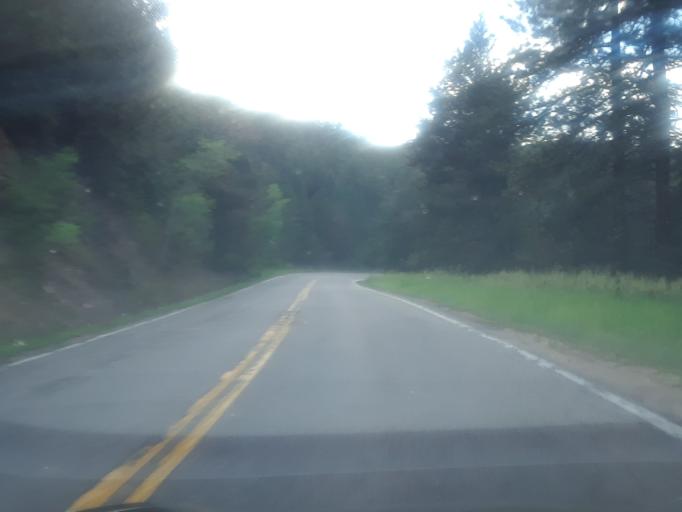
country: US
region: Colorado
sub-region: Jefferson County
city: Kittredge
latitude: 39.7123
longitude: -105.3499
